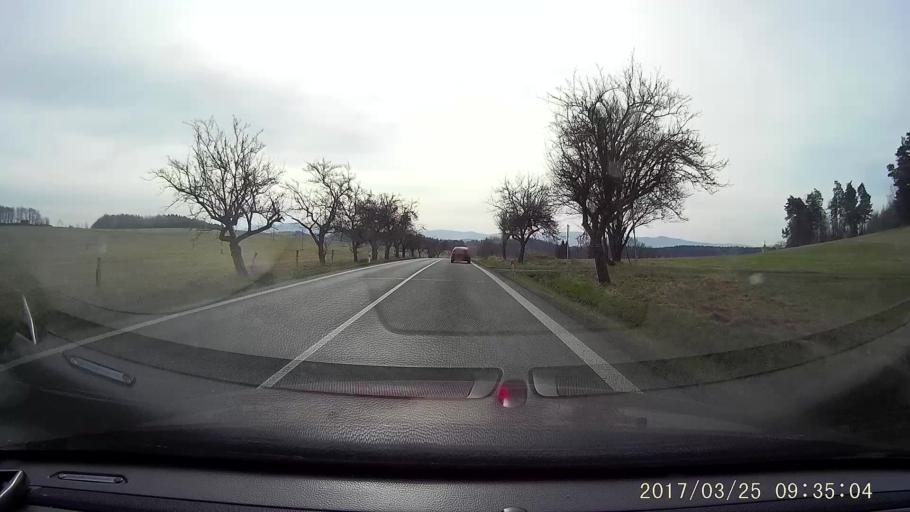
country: CZ
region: Liberecky
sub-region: Okres Liberec
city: Frydlant
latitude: 50.9678
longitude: 15.0956
